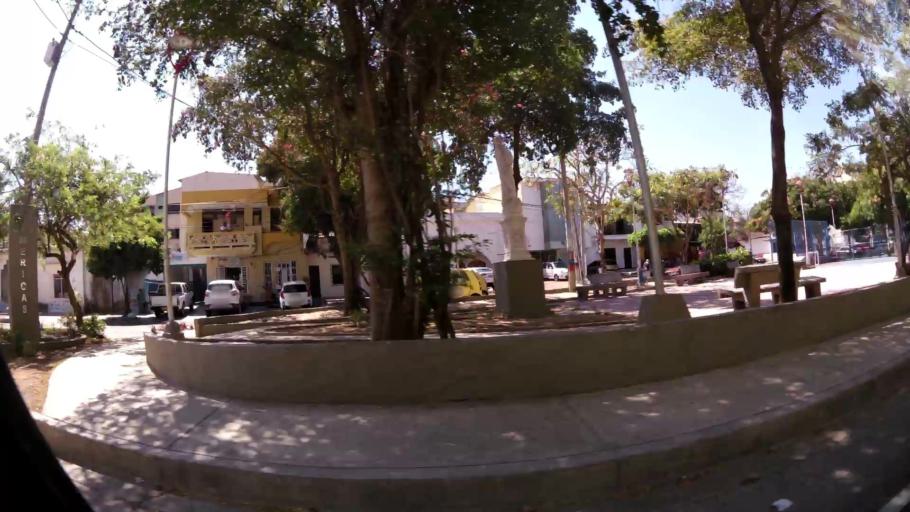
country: CO
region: Atlantico
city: Barranquilla
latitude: 10.9938
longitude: -74.7974
